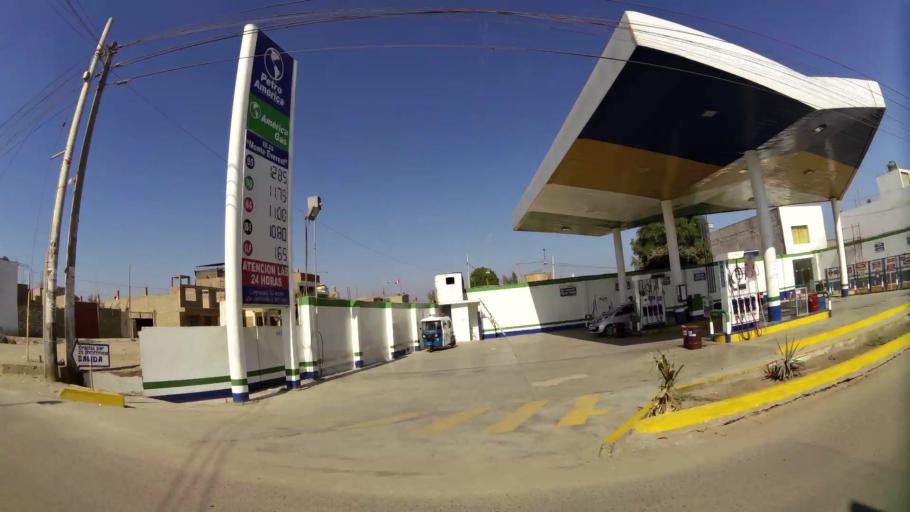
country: PE
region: Ica
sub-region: Provincia de Chincha
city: Chincha Alta
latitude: -13.4123
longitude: -76.1266
